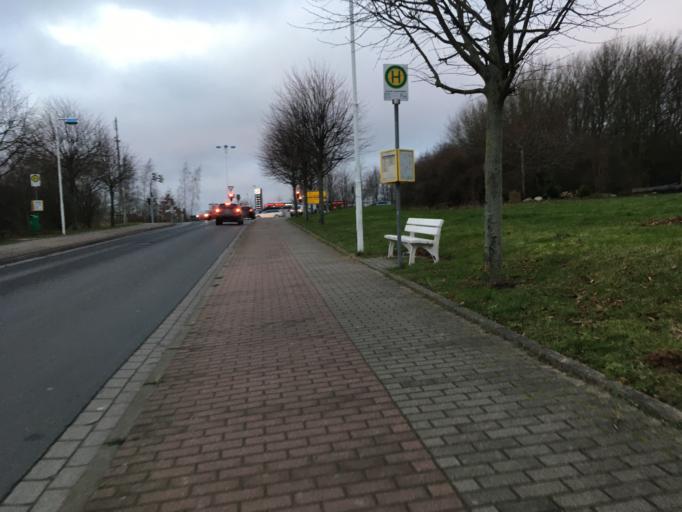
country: DE
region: Mecklenburg-Vorpommern
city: Sassnitz
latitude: 54.5122
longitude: 13.6050
